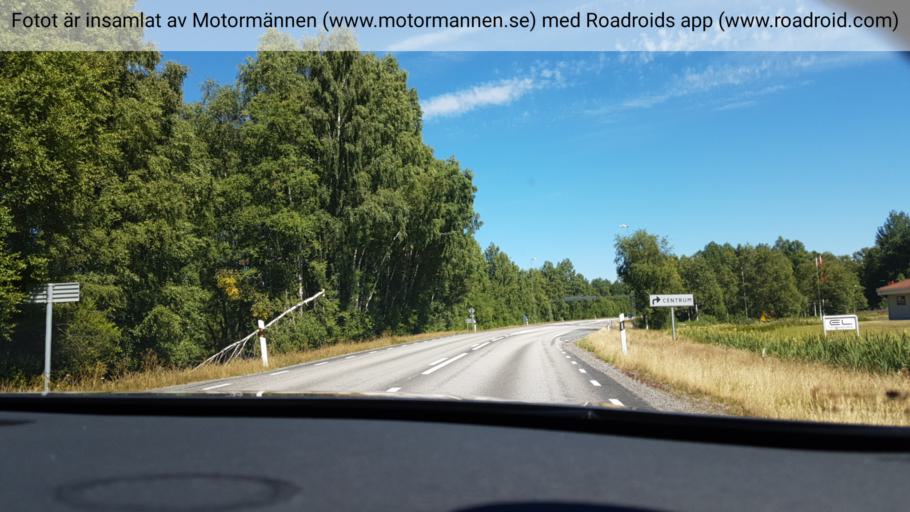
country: SE
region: Joenkoeping
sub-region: Gnosjo Kommun
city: Hillerstorp
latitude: 57.3218
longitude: 13.8740
